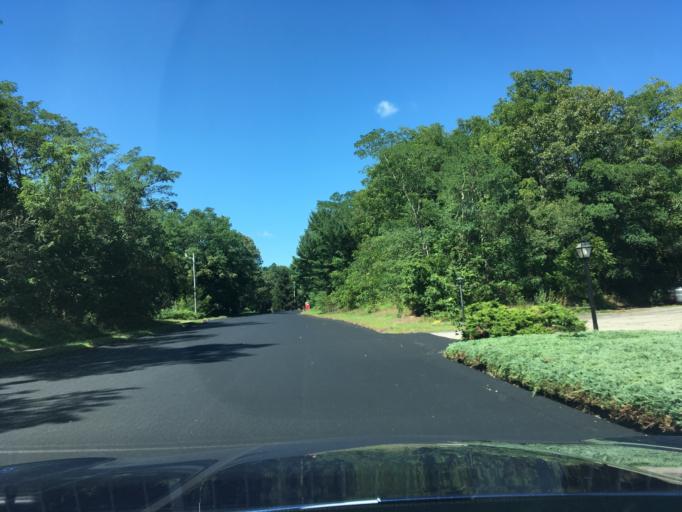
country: US
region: Rhode Island
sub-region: Kent County
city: East Greenwich
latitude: 41.6355
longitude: -71.4685
